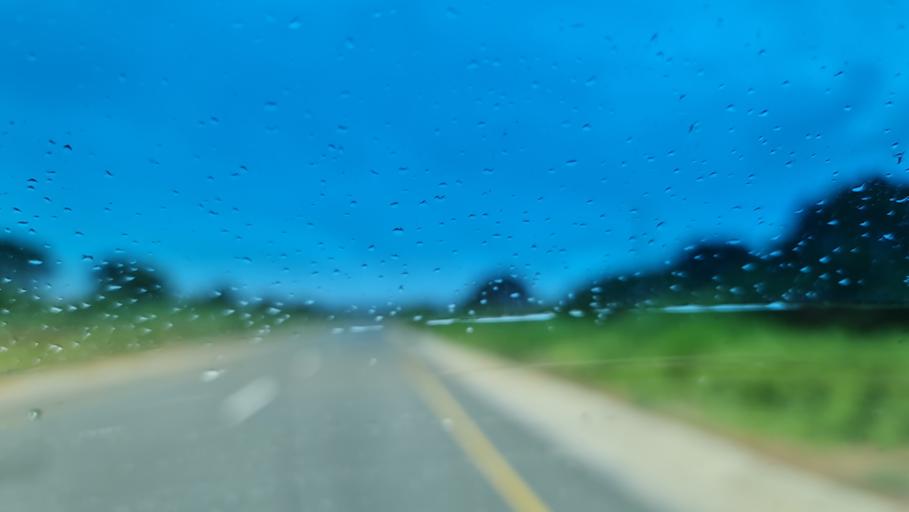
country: MZ
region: Nampula
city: Nampula
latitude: -15.5054
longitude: 39.3326
